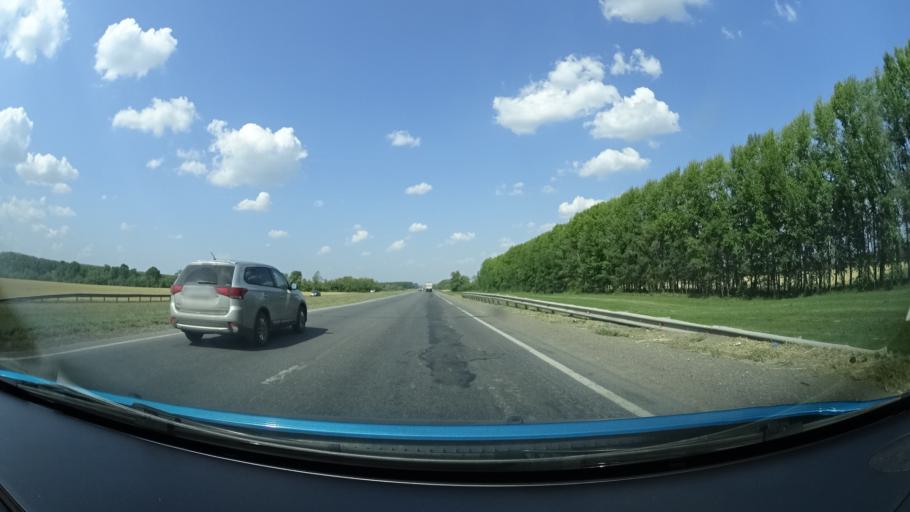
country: RU
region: Bashkortostan
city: Chishmy
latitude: 54.6575
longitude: 55.4729
